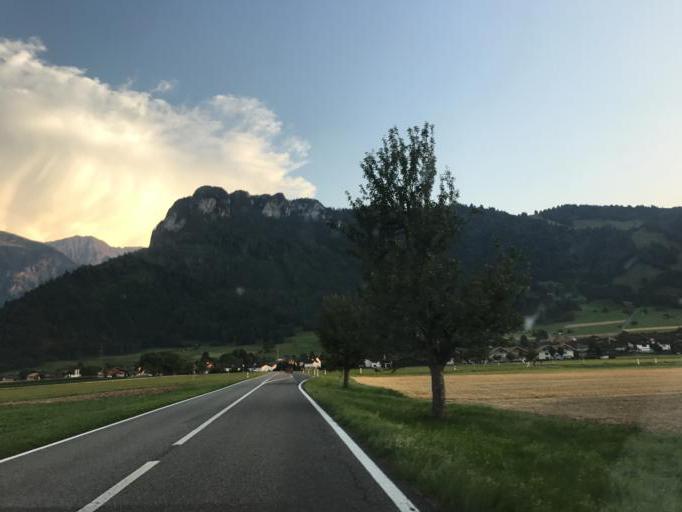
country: CH
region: Bern
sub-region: Frutigen-Niedersimmental District
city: Wimmis
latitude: 46.7000
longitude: 7.6274
